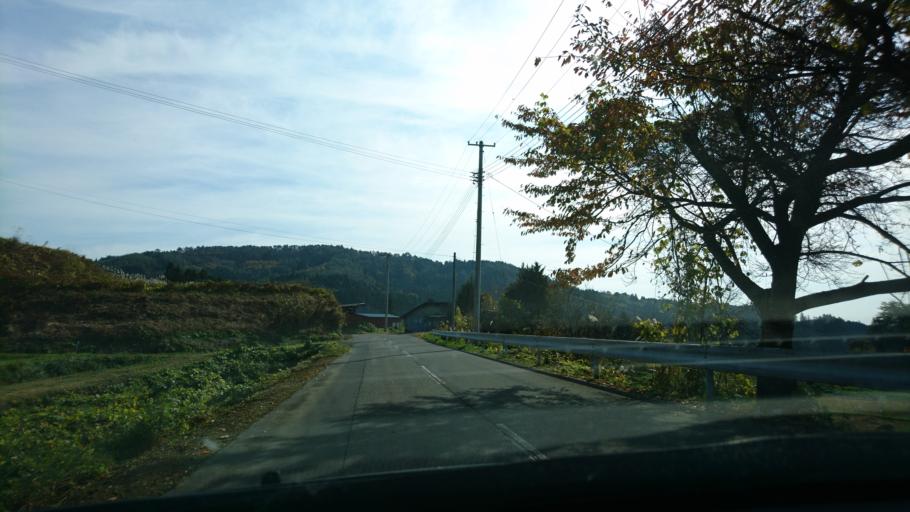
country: JP
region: Iwate
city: Ichinoseki
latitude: 38.9768
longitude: 141.1779
